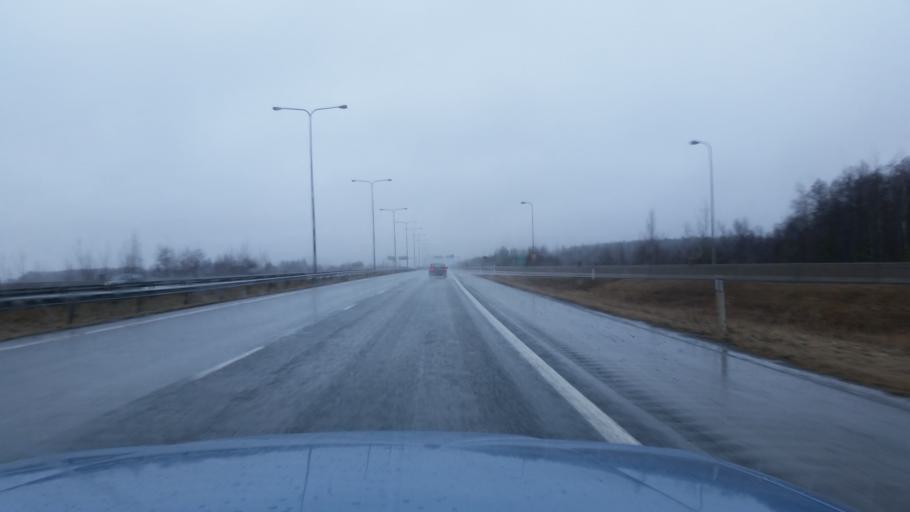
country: FI
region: Pirkanmaa
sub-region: Etelae-Pirkanmaa
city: Toijala
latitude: 61.2100
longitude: 23.8391
